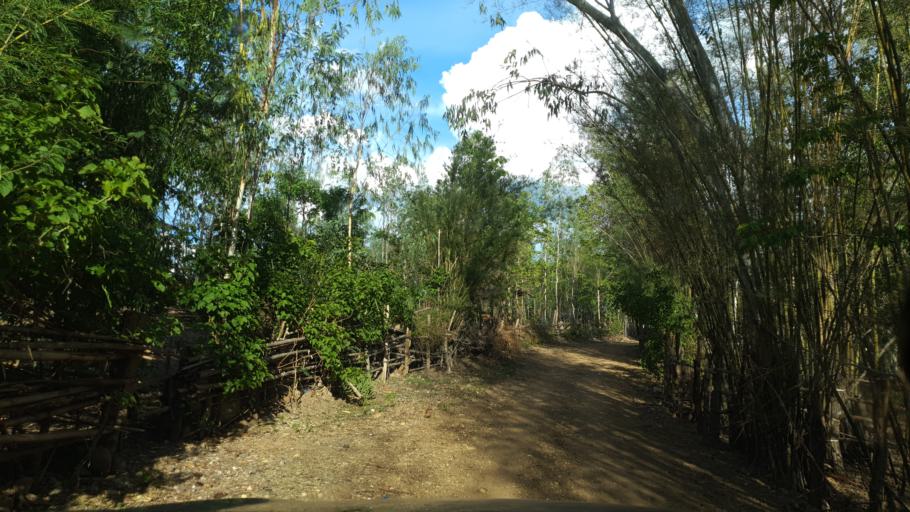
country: TH
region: Lampang
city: Sop Prap
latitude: 17.8815
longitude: 99.2955
